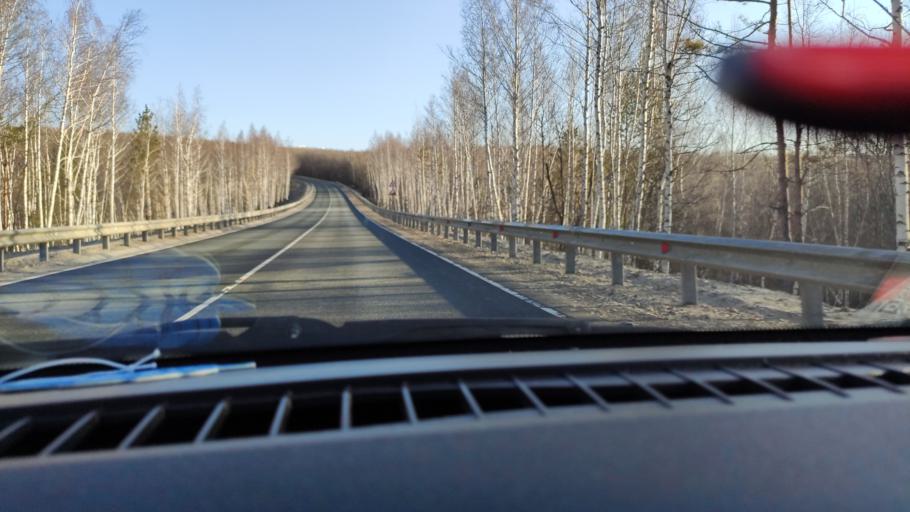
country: RU
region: Saratov
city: Khvalynsk
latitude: 52.4611
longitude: 48.0173
